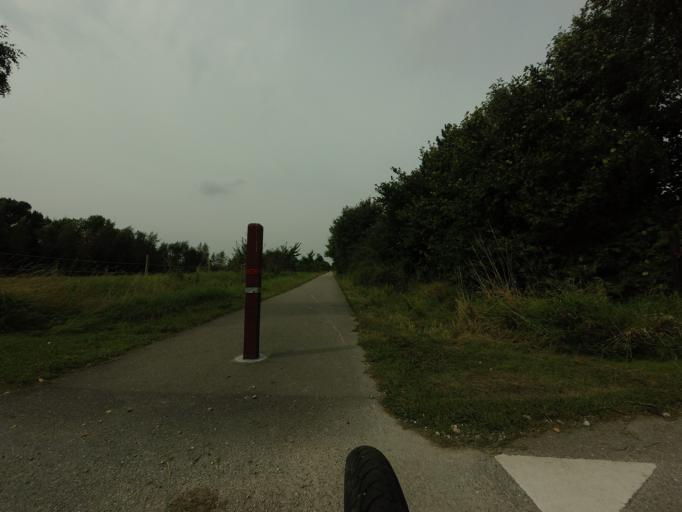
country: DK
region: Zealand
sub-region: Naestved Kommune
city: Fuglebjerg
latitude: 55.2632
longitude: 11.5427
